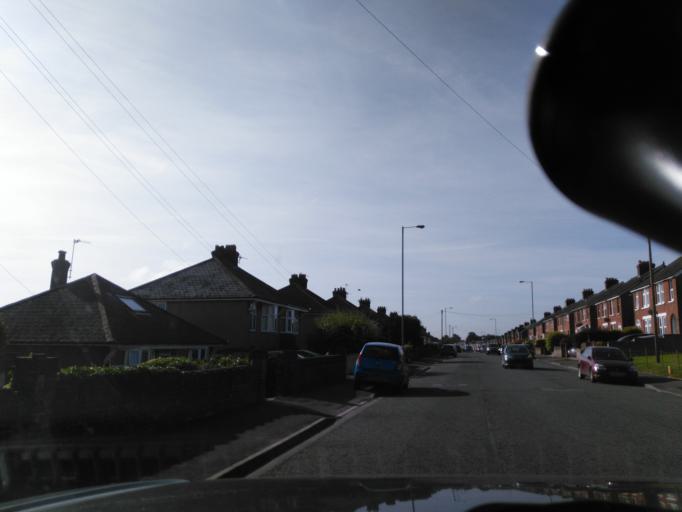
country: GB
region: England
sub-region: Wiltshire
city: Salisbury
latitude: 51.0848
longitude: -1.8217
